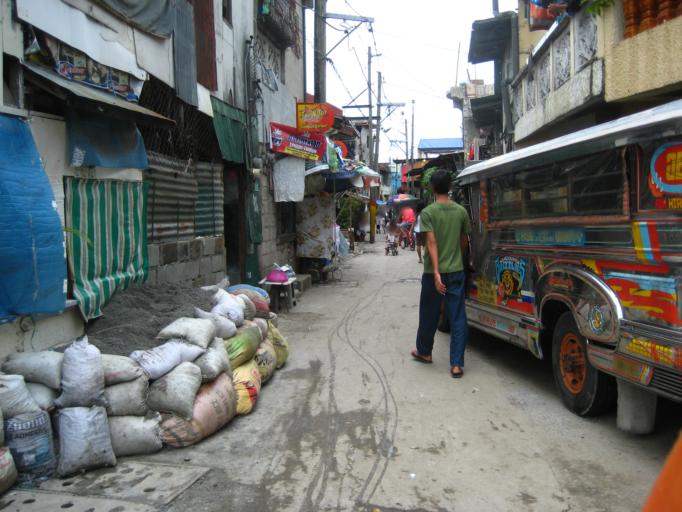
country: PH
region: Calabarzon
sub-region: Province of Rizal
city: Pateros
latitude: 14.5425
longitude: 121.0705
